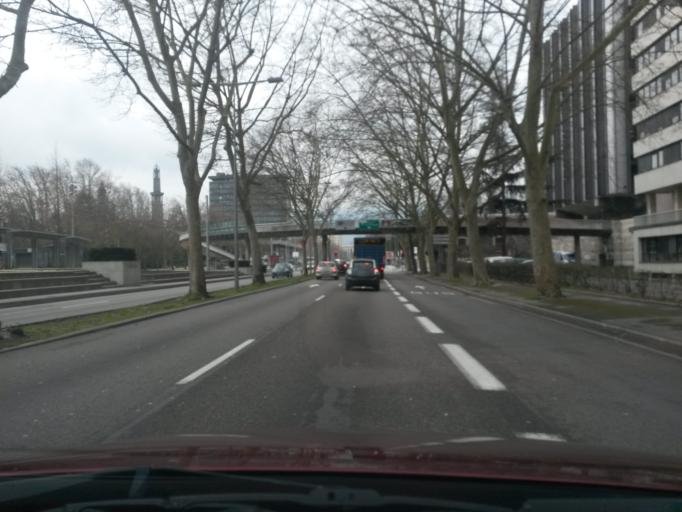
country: FR
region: Rhone-Alpes
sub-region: Departement de l'Isere
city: La Tronche
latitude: 45.1883
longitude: 5.7392
